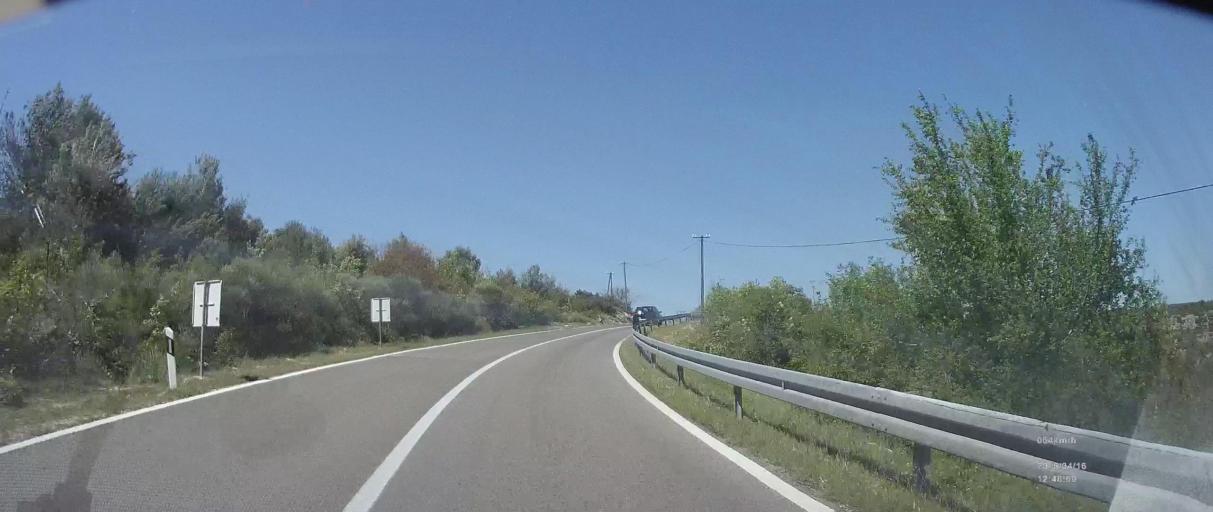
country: HR
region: Sibensko-Kniniska
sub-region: Grad Sibenik
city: Brodarica
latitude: 43.6687
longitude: 16.0432
